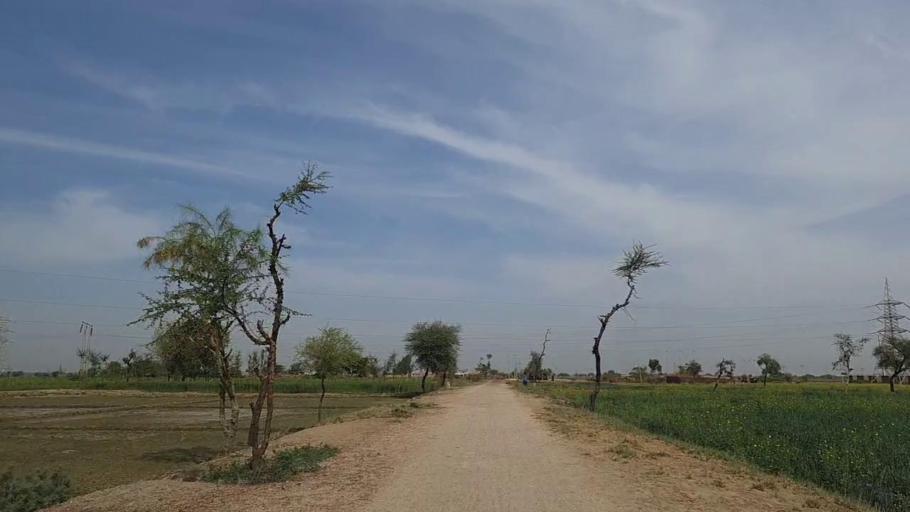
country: PK
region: Sindh
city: Samaro
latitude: 25.2906
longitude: 69.4123
